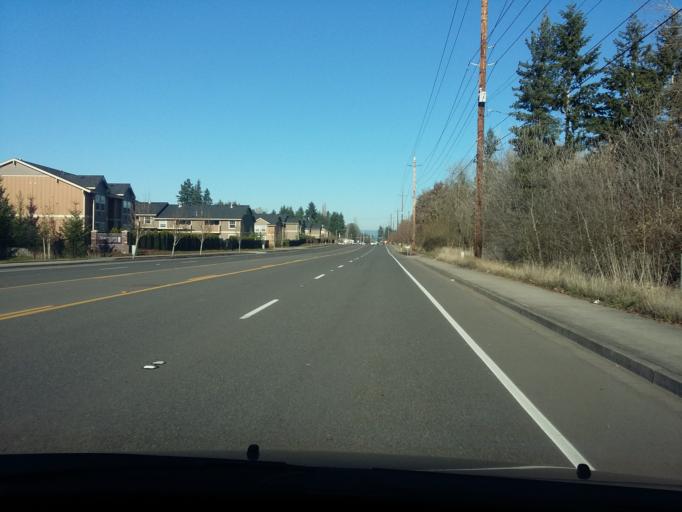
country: US
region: Washington
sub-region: Clark County
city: Barberton
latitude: 45.6972
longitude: -122.5992
